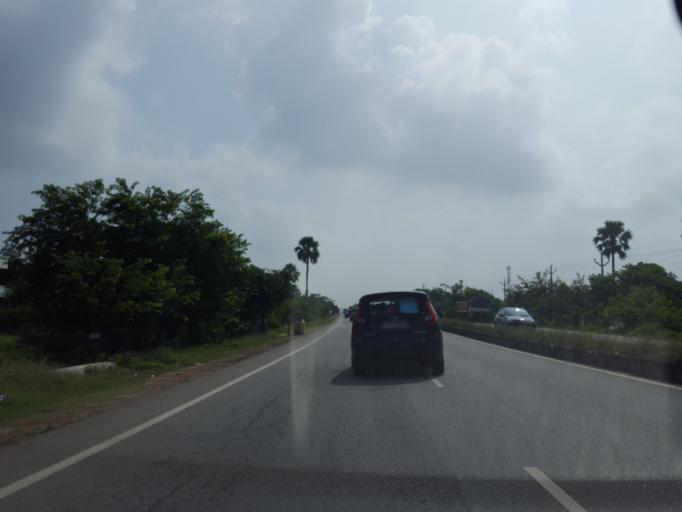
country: IN
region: Telangana
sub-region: Rangareddi
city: Ghatkesar
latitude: 17.2934
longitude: 78.7484
